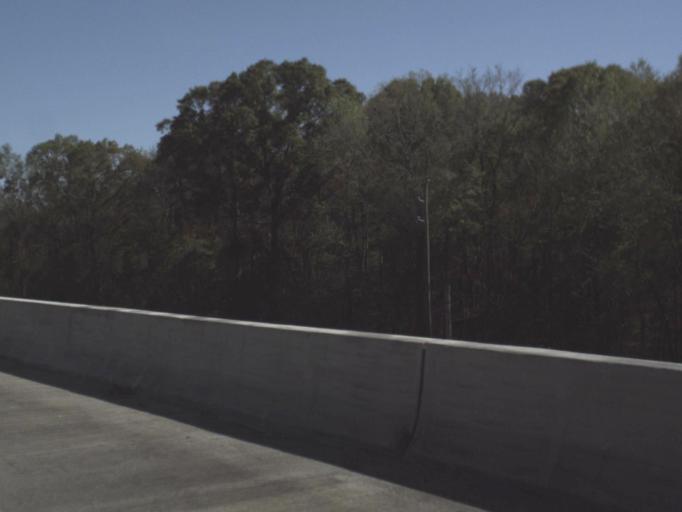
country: US
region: Florida
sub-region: Holmes County
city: Bonifay
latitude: 30.7767
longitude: -85.8292
